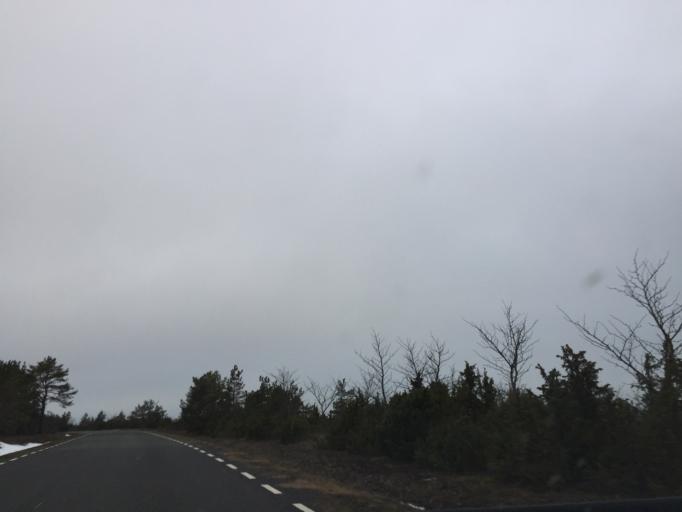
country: EE
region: Saare
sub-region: Kuressaare linn
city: Kuressaare
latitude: 58.5652
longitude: 22.3101
